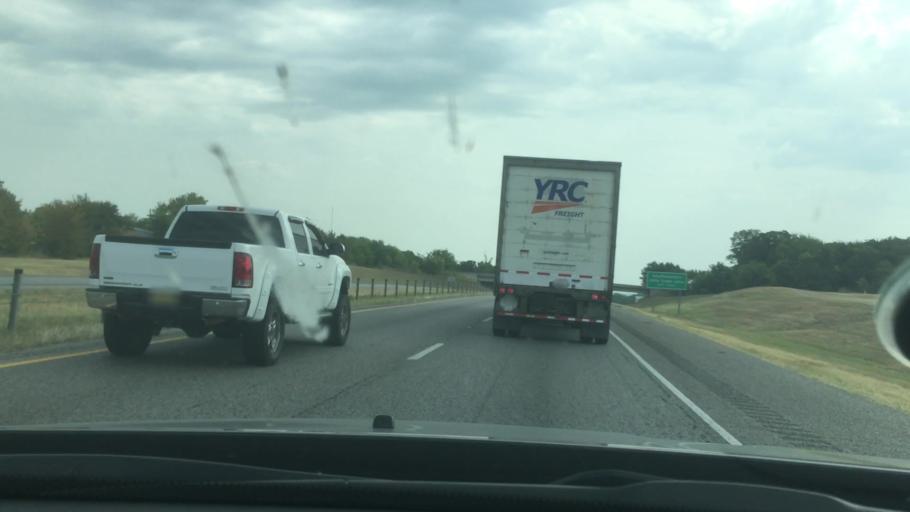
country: US
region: Oklahoma
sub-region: Bryan County
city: Durant
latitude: 34.0314
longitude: -96.3820
